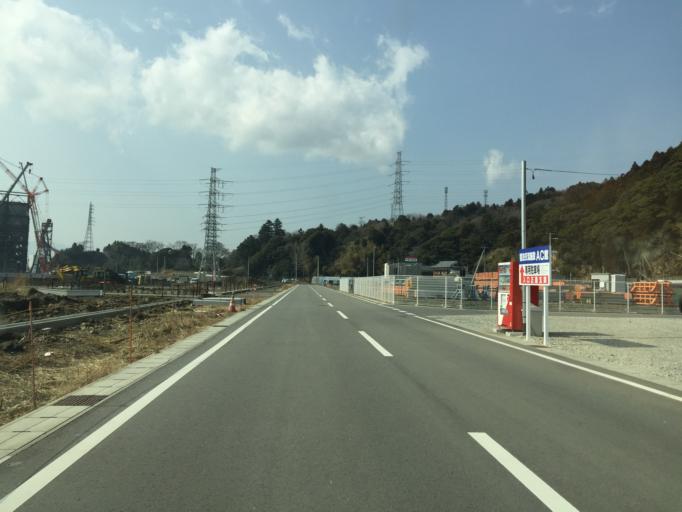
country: JP
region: Fukushima
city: Iwaki
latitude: 36.9150
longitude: 140.8241
